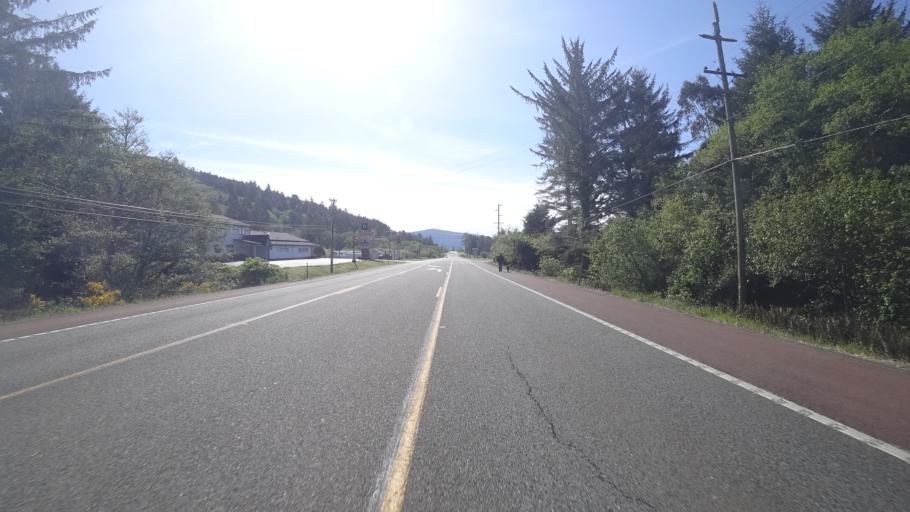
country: US
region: Oregon
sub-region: Curry County
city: Harbor
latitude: 41.9490
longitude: -124.1988
